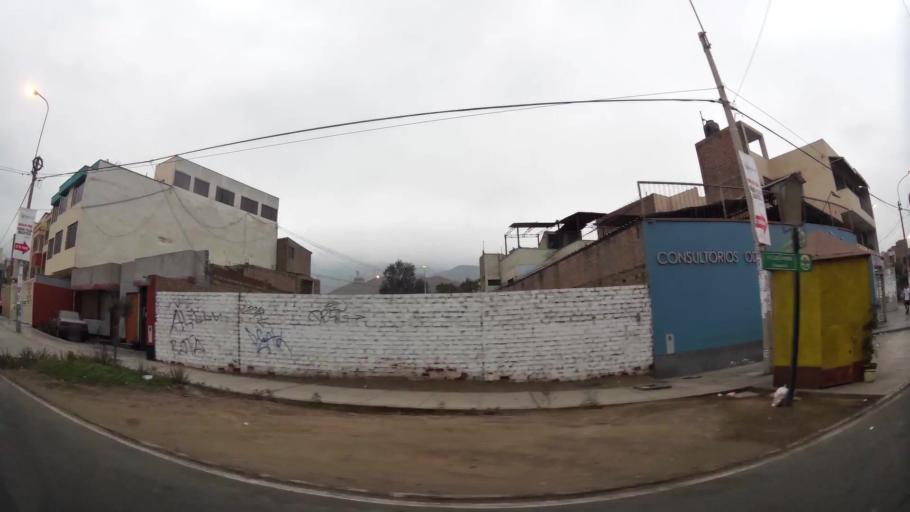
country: PE
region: Lima
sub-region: Lima
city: La Molina
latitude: -12.1009
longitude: -76.9435
